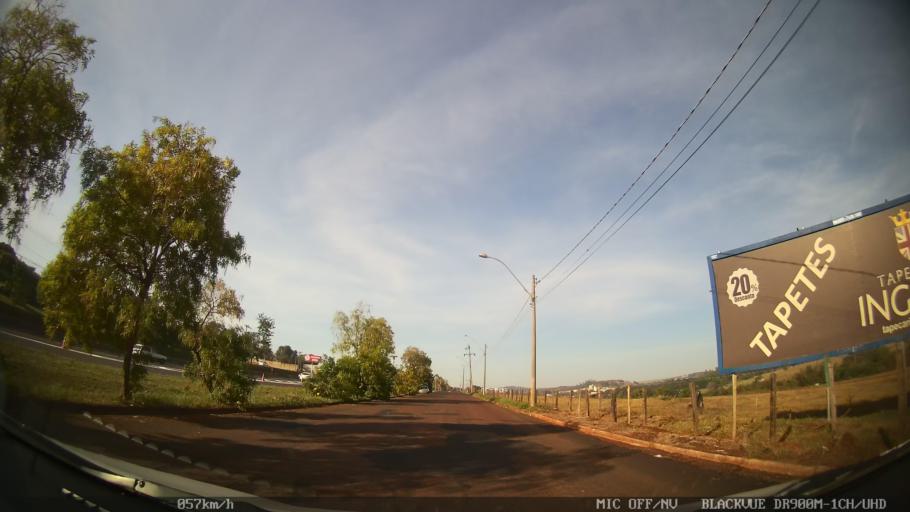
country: BR
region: Sao Paulo
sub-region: Ribeirao Preto
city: Ribeirao Preto
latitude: -21.2519
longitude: -47.8196
